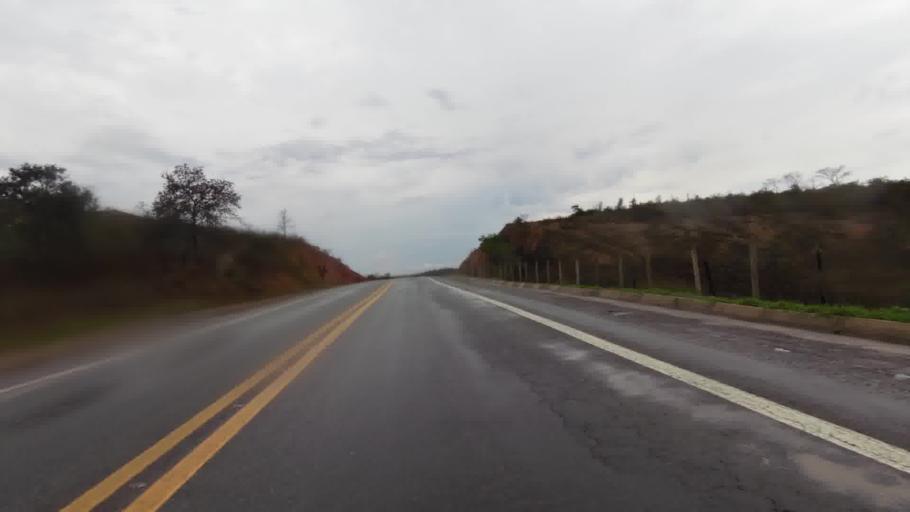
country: BR
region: Rio de Janeiro
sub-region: Campos Dos Goytacazes
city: Campos
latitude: -21.4867
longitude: -41.3405
